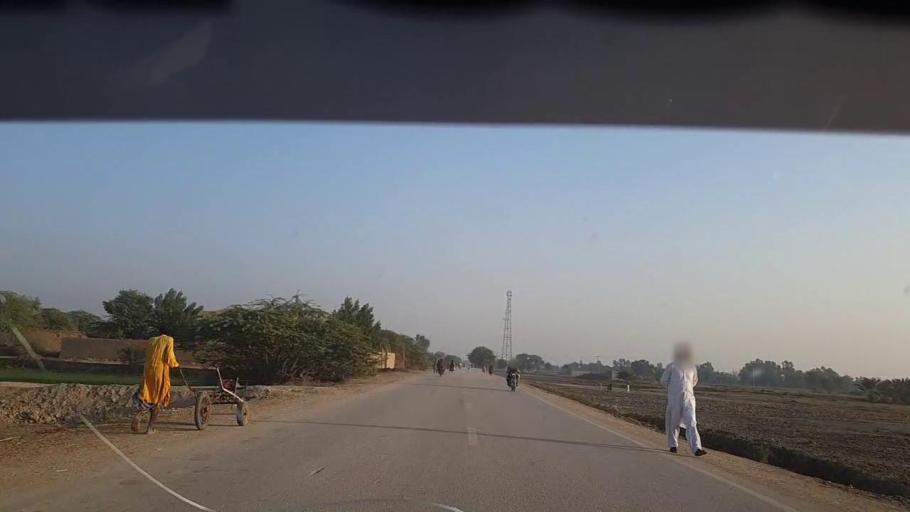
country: PK
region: Sindh
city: Ranipur
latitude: 27.2700
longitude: 68.5180
